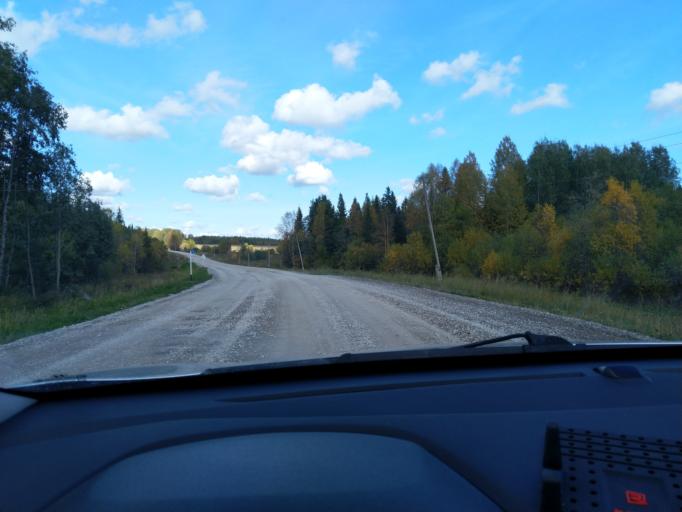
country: RU
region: Perm
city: Usol'ye
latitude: 59.4646
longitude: 56.3698
